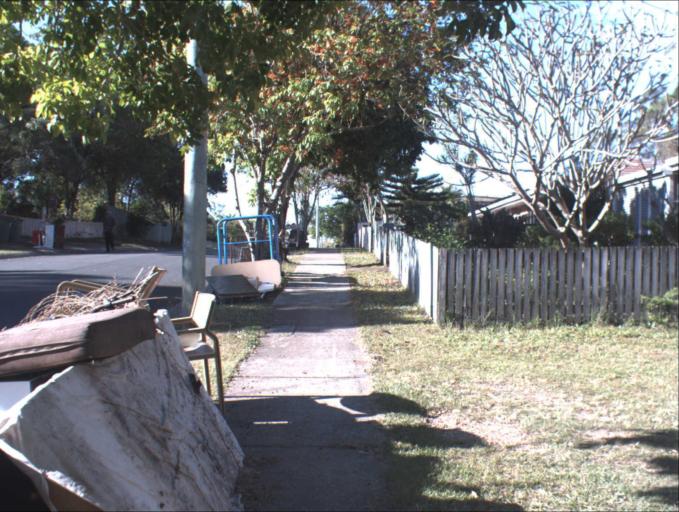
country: AU
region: Queensland
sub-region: Logan
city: Slacks Creek
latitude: -27.6505
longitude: 153.1316
